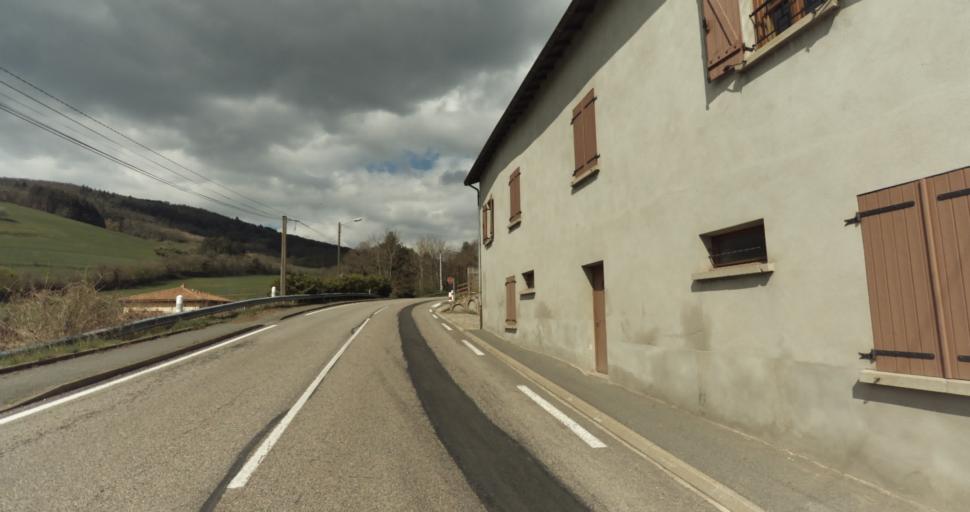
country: FR
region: Rhone-Alpes
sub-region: Departement du Rhone
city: Tarare
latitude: 45.9136
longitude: 4.4223
